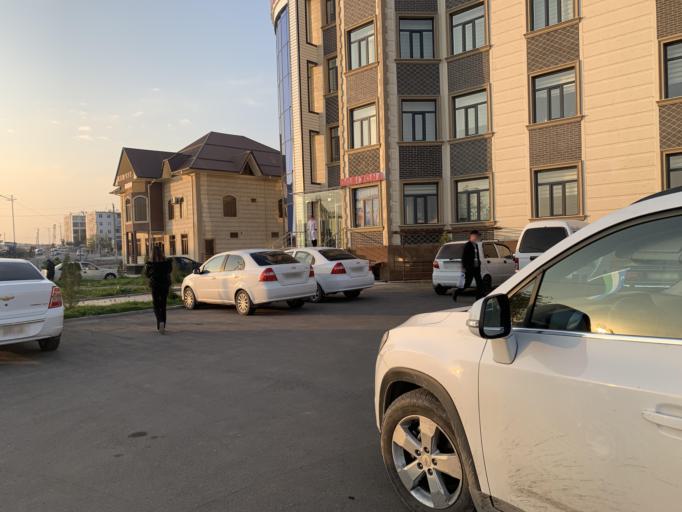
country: UZ
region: Namangan
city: Namangan Shahri
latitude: 41.0020
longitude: 71.5997
